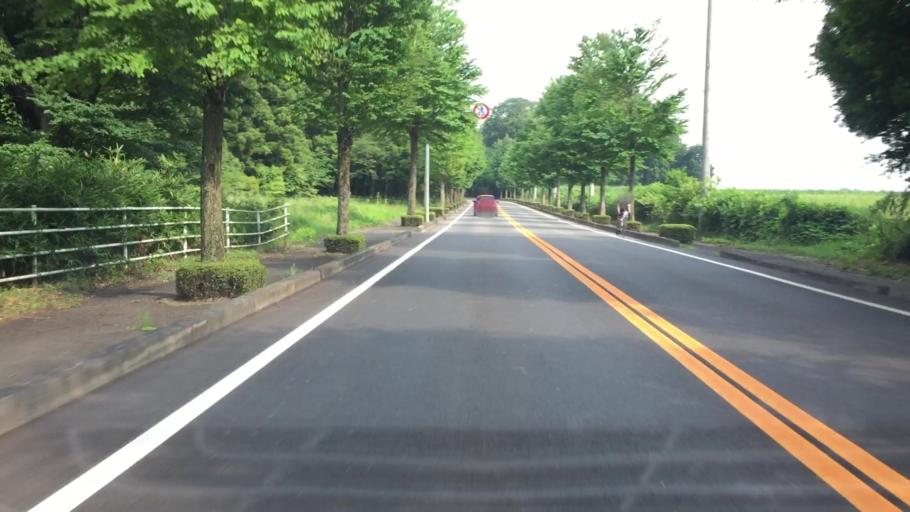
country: JP
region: Tochigi
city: Kuroiso
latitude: 36.9816
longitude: 139.9615
